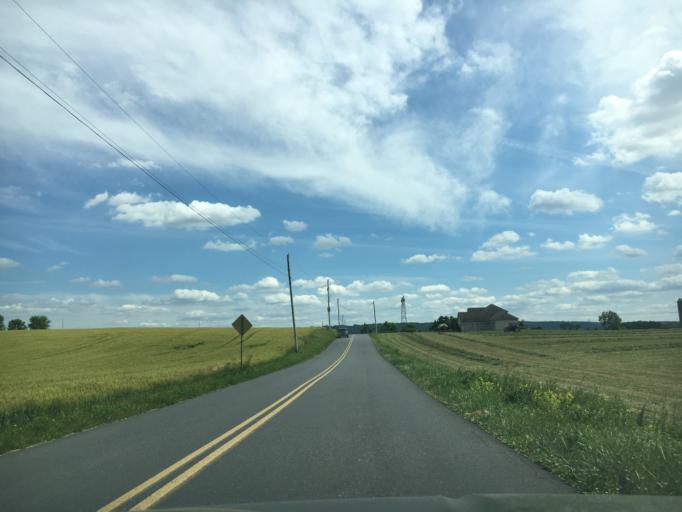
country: US
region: Pennsylvania
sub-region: Berks County
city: Kutztown
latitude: 40.4926
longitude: -75.7889
